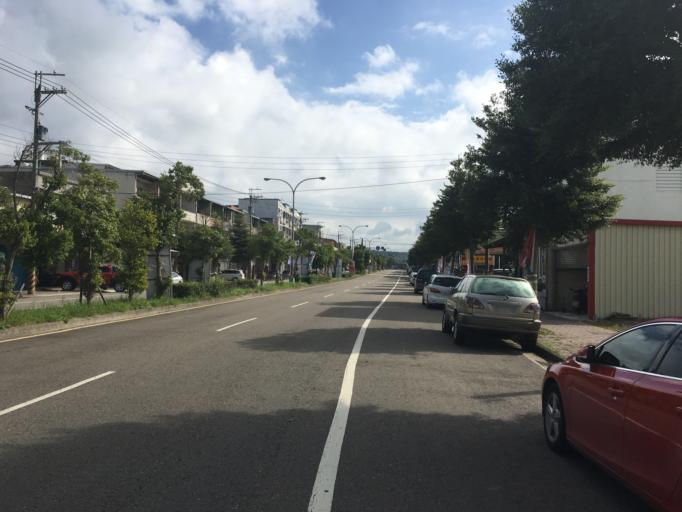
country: TW
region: Taiwan
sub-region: Hsinchu
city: Zhubei
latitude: 24.8902
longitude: 121.0513
